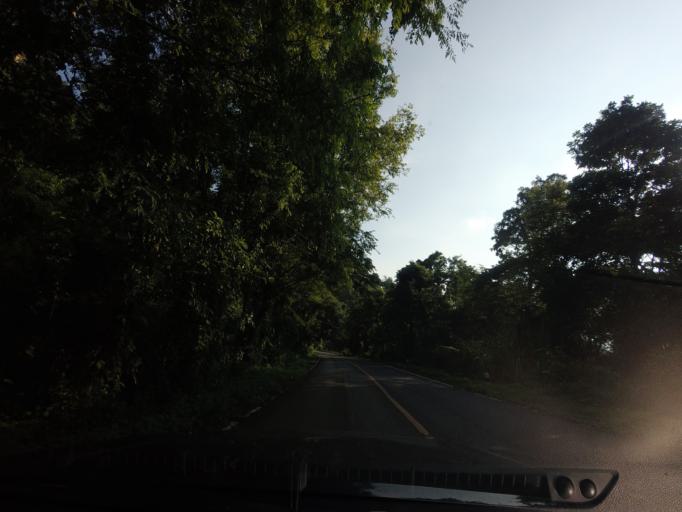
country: TH
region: Nan
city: Na Noi
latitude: 18.3654
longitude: 100.8270
